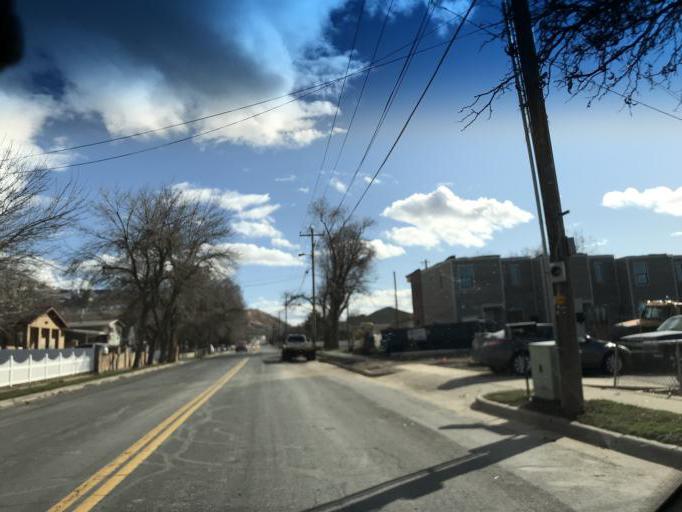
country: US
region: Utah
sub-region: Davis County
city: North Salt Lake
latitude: 40.8451
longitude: -111.9118
